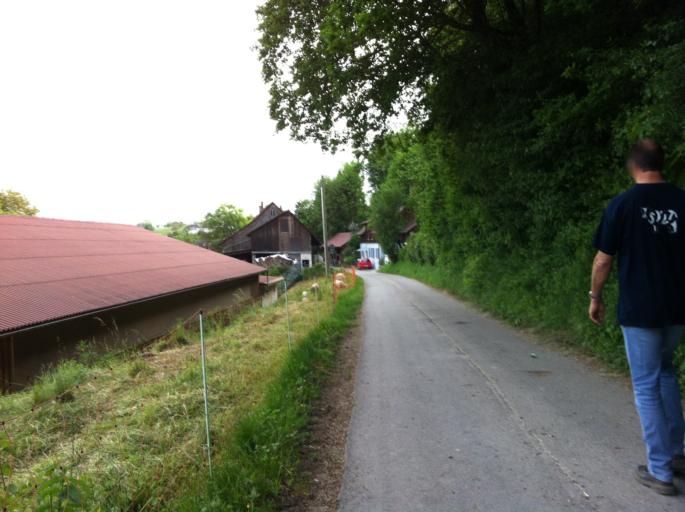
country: DE
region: Baden-Wuerttemberg
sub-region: Freiburg Region
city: Maulburg
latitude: 47.6070
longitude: 7.7918
